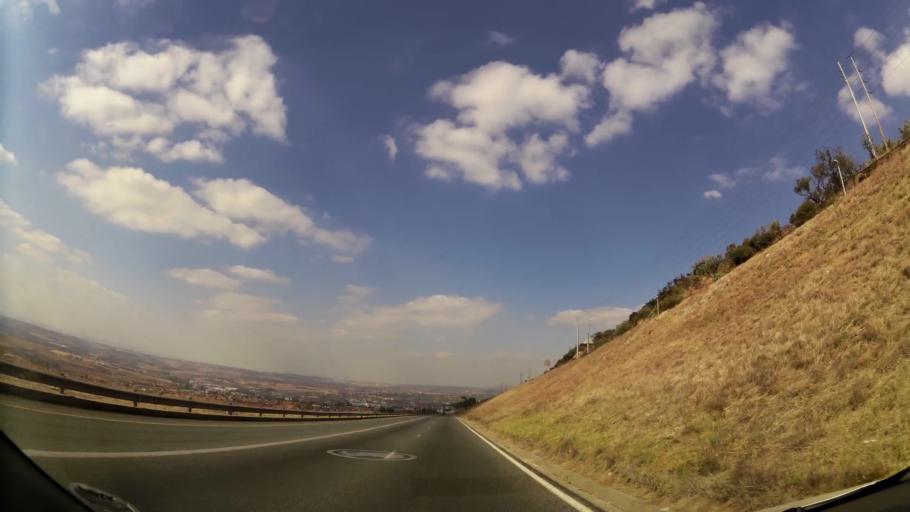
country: ZA
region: Gauteng
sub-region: West Rand District Municipality
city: Muldersdriseloop
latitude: -26.0628
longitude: 27.8110
